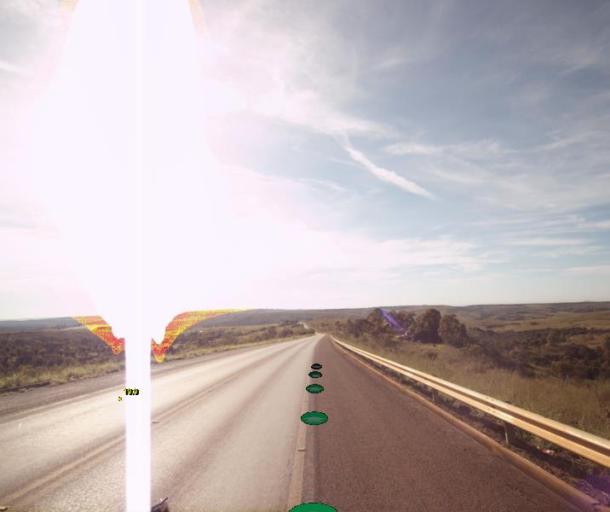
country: BR
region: Federal District
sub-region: Brasilia
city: Brasilia
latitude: -15.7426
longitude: -48.3744
